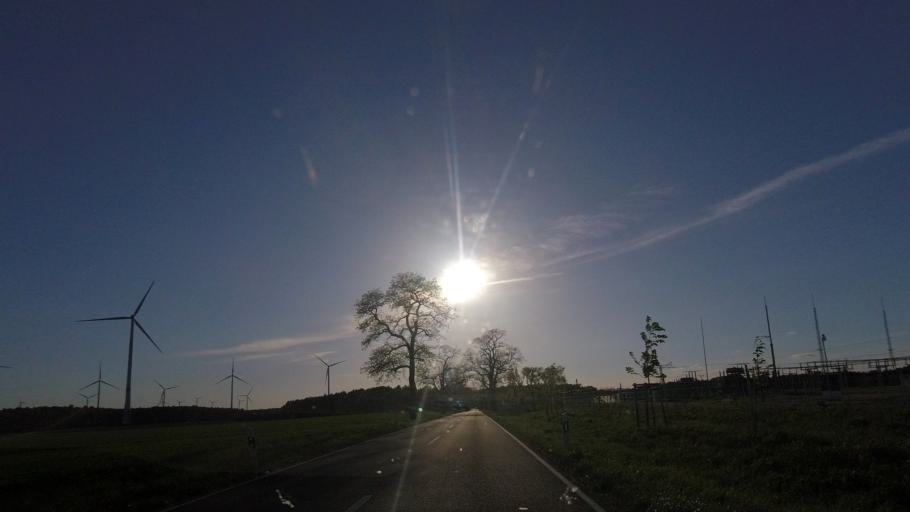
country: DE
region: Brandenburg
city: Ihlow
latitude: 51.9857
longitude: 13.3430
